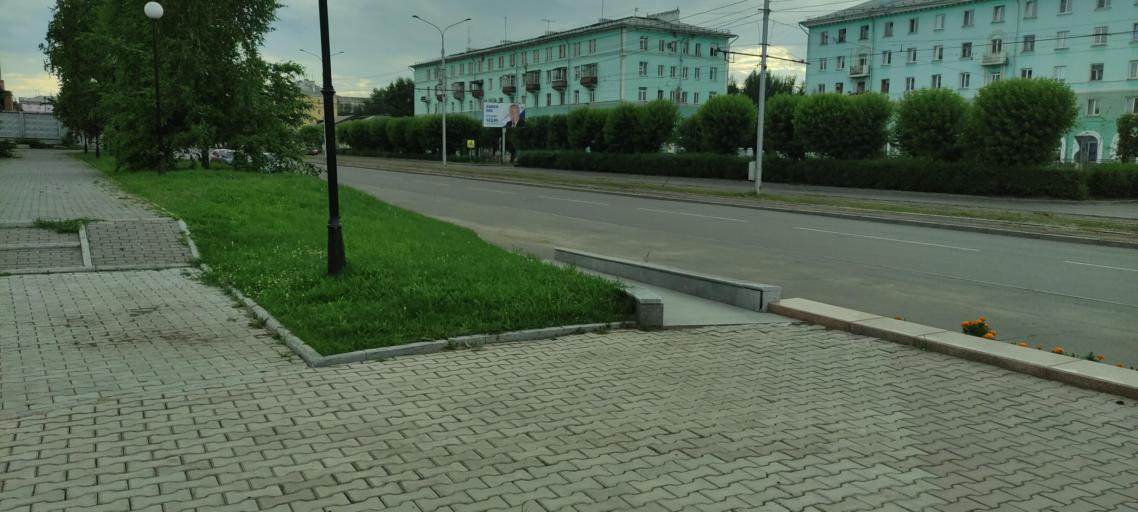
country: RU
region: Krasnoyarskiy
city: Krasnoyarsk
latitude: 56.0144
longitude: 92.9790
